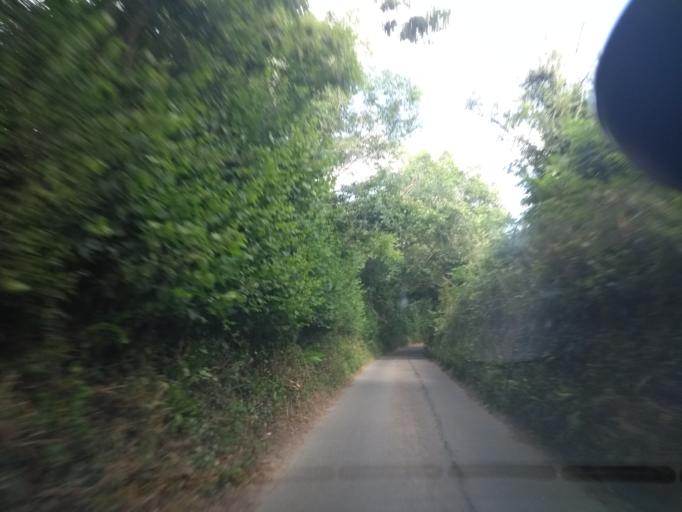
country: GB
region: England
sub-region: Devon
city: Modbury
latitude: 50.3068
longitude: -3.8565
